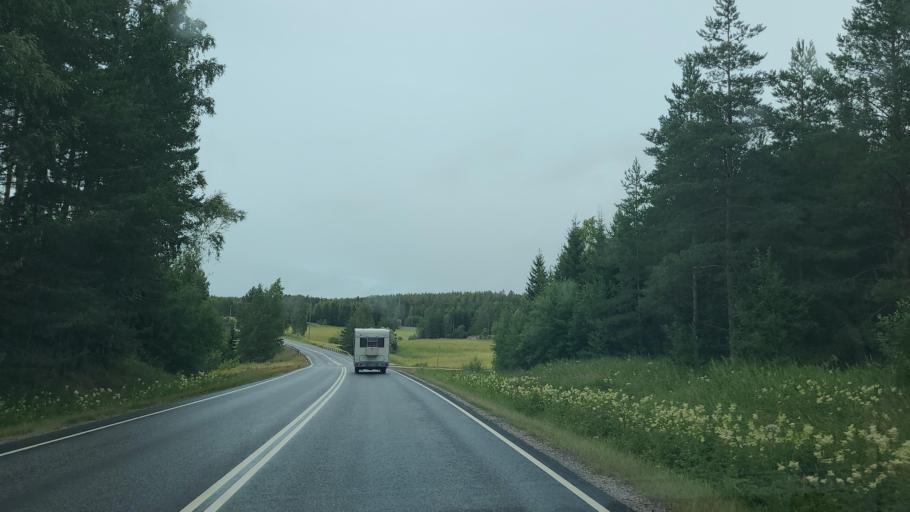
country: FI
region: Varsinais-Suomi
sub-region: Turku
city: Sauvo
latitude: 60.2717
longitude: 22.6689
